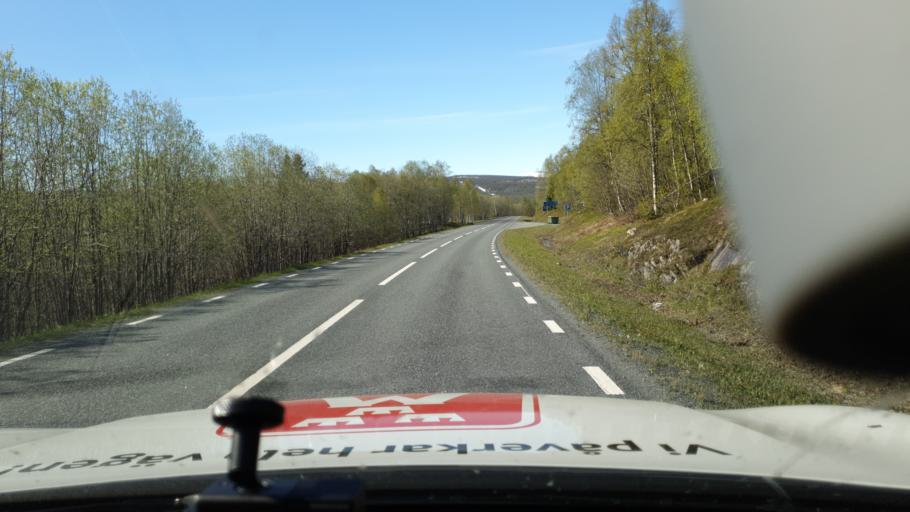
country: NO
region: Nordland
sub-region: Rana
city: Mo i Rana
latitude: 65.7575
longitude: 15.1148
